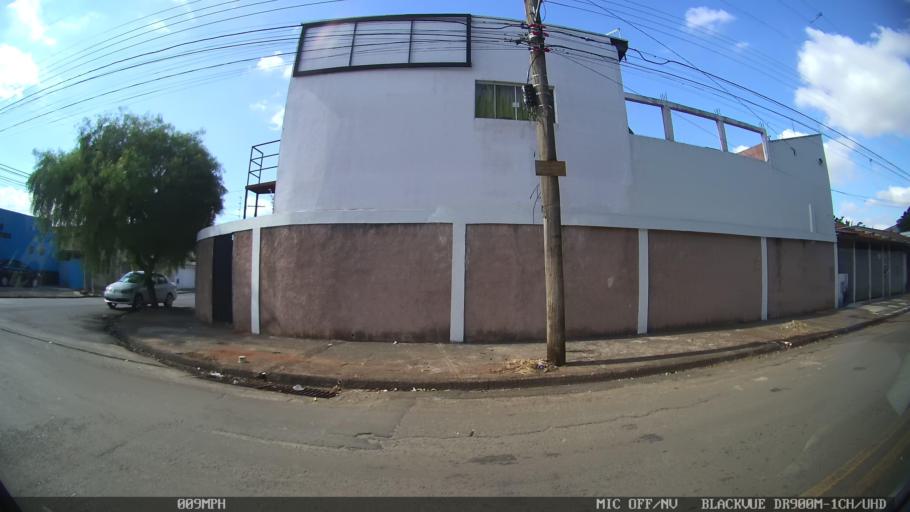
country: BR
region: Sao Paulo
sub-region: Hortolandia
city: Hortolandia
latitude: -22.8777
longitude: -47.2062
